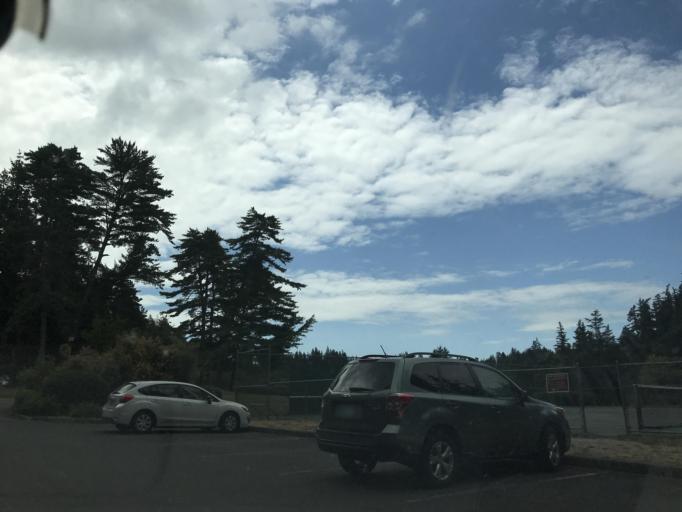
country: US
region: Washington
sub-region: Whatcom County
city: Bellingham
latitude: 48.7148
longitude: -122.4978
